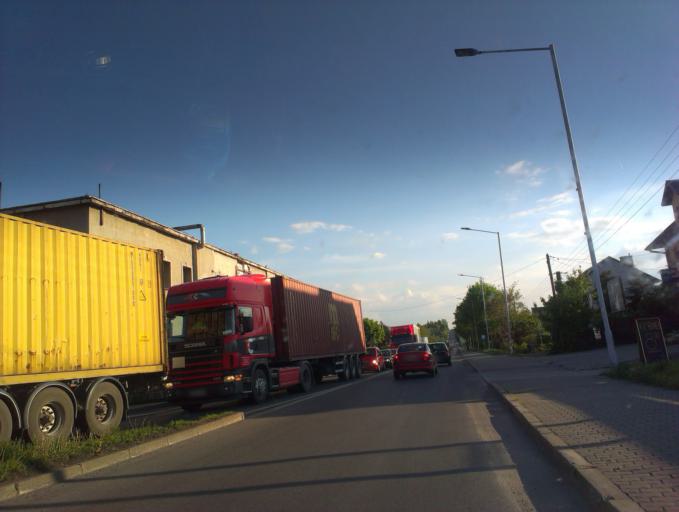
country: PL
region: Swietokrzyskie
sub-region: Powiat ostrowiecki
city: Ostrowiec Swietokrzyski
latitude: 50.9246
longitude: 21.3982
